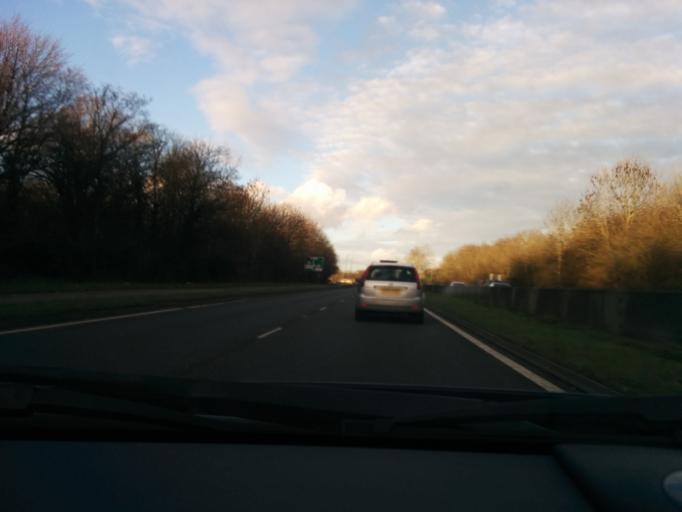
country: GB
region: England
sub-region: Oxfordshire
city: Cowley
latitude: 51.7555
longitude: -1.1950
